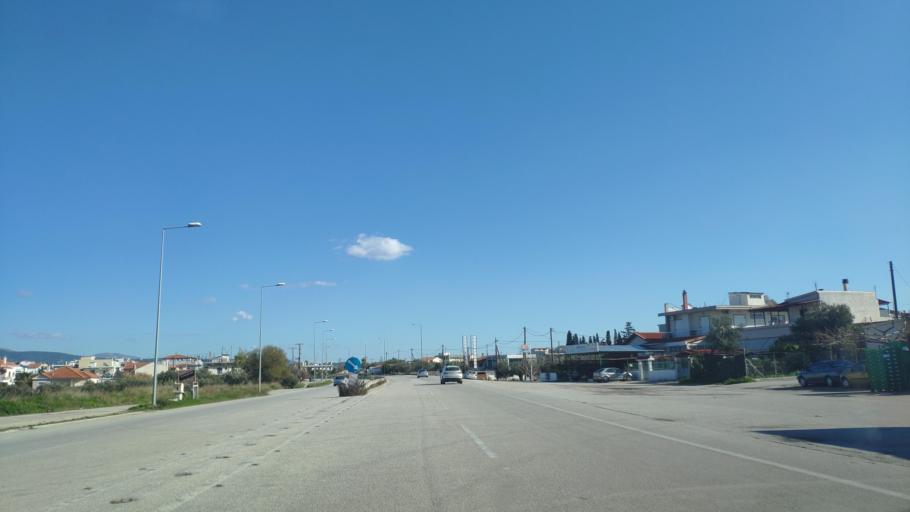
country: GR
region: Peloponnese
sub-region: Nomos Korinthias
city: Korinthos
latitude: 37.9341
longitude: 22.9415
